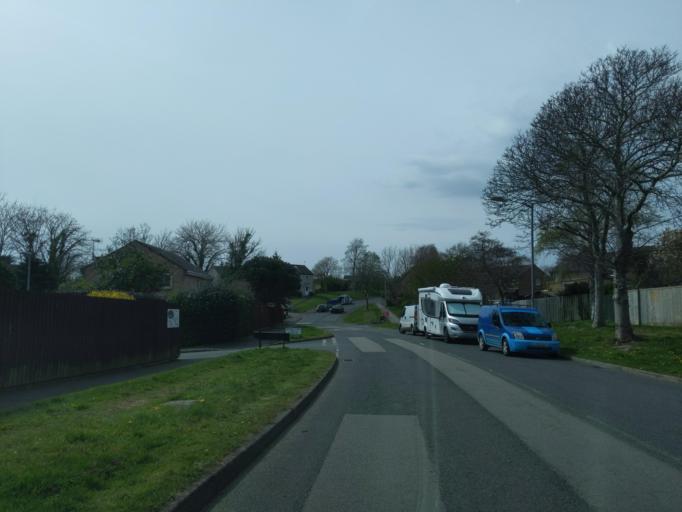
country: GB
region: England
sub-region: Cornwall
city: Torpoint
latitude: 50.3769
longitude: -4.2185
